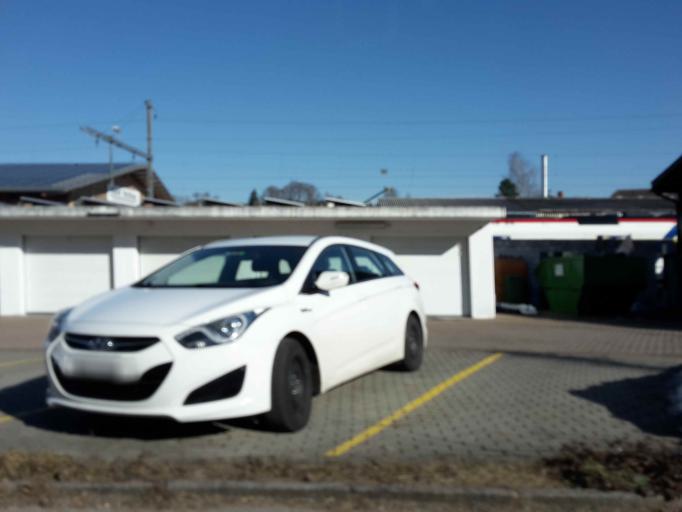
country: CH
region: Bern
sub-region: Emmental District
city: Sumiswald
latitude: 47.0616
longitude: 7.7496
